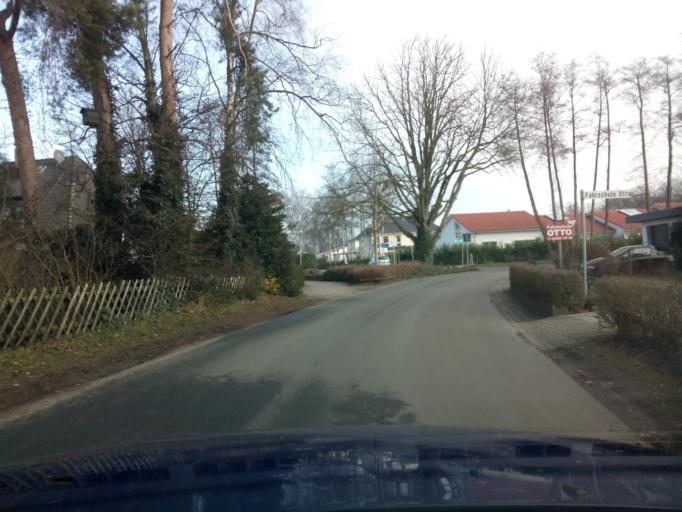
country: DE
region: Lower Saxony
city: Lilienthal
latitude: 53.1518
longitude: 8.9077
